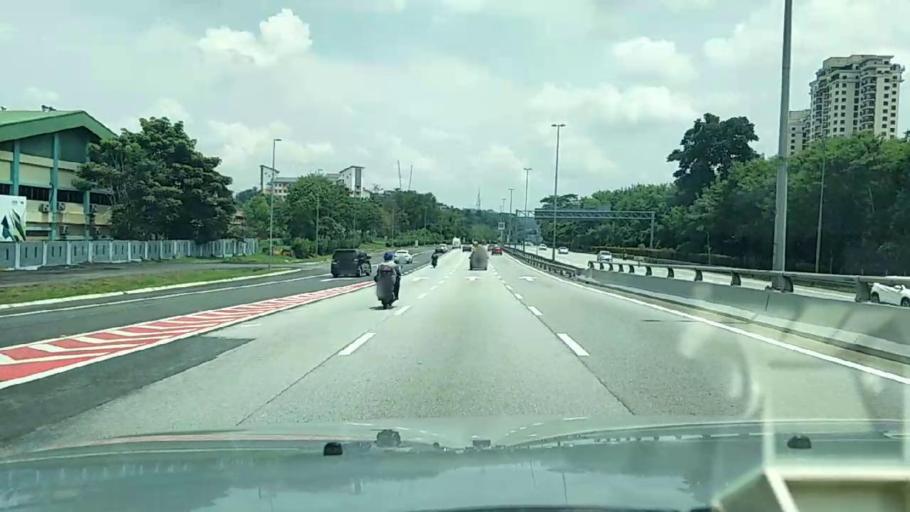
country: MY
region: Kuala Lumpur
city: Kuala Lumpur
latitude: 3.0942
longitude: 101.6869
